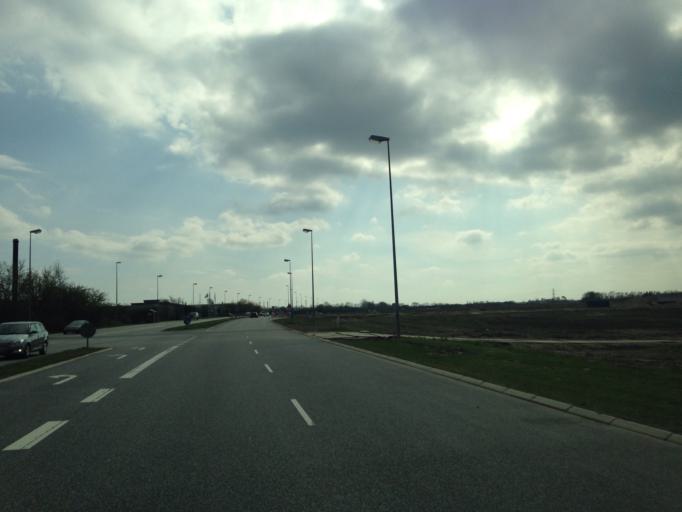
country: DK
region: Capital Region
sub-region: Ishoj Kommune
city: Ishoj
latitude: 55.6185
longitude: 12.3174
